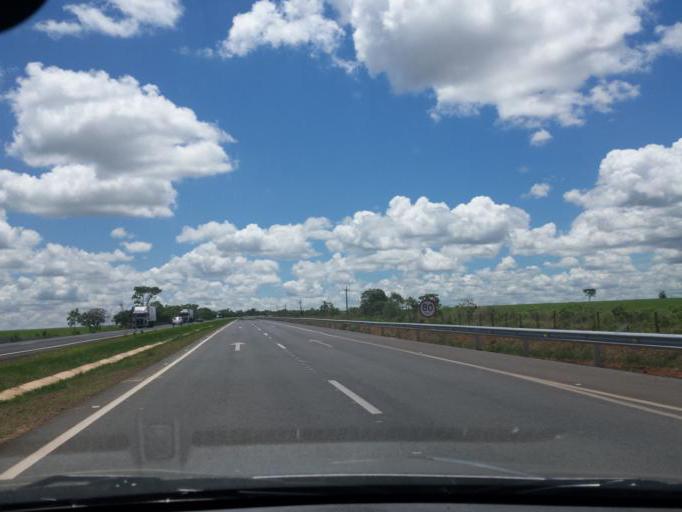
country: BR
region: Goias
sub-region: Cristalina
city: Cristalina
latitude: -16.6653
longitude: -47.7183
